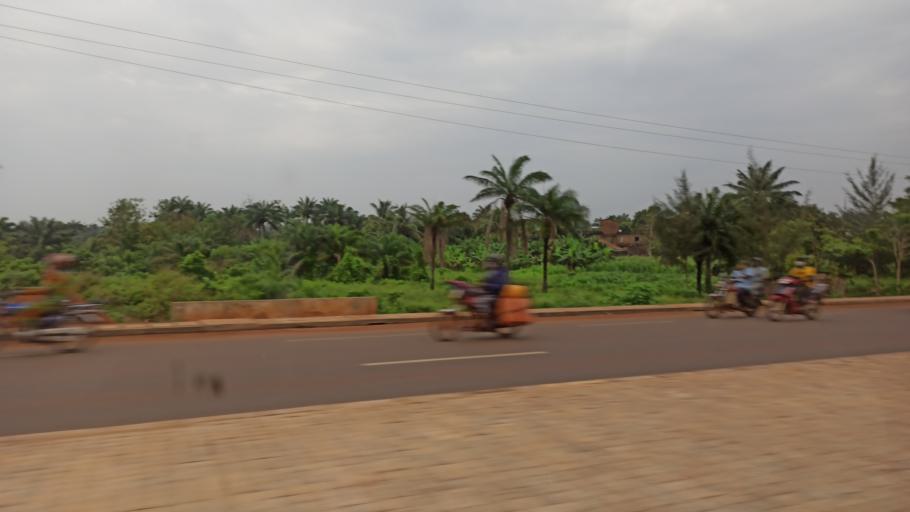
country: BJ
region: Queme
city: Porto-Novo
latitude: 6.5322
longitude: 2.5993
